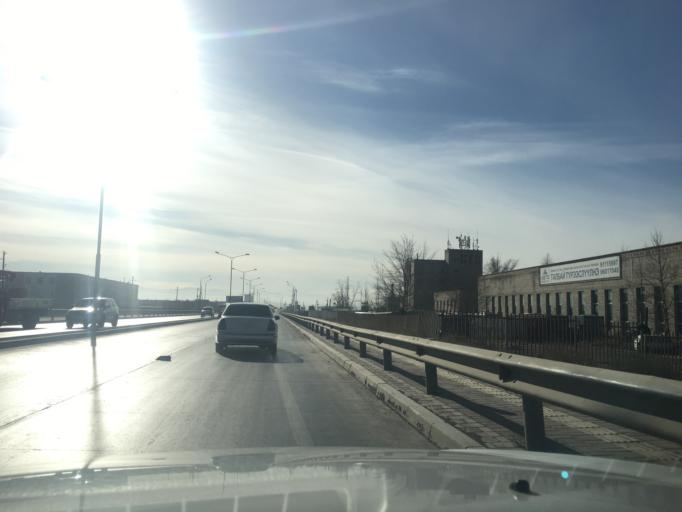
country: MN
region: Ulaanbaatar
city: Ulaanbaatar
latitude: 47.9043
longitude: 106.7858
